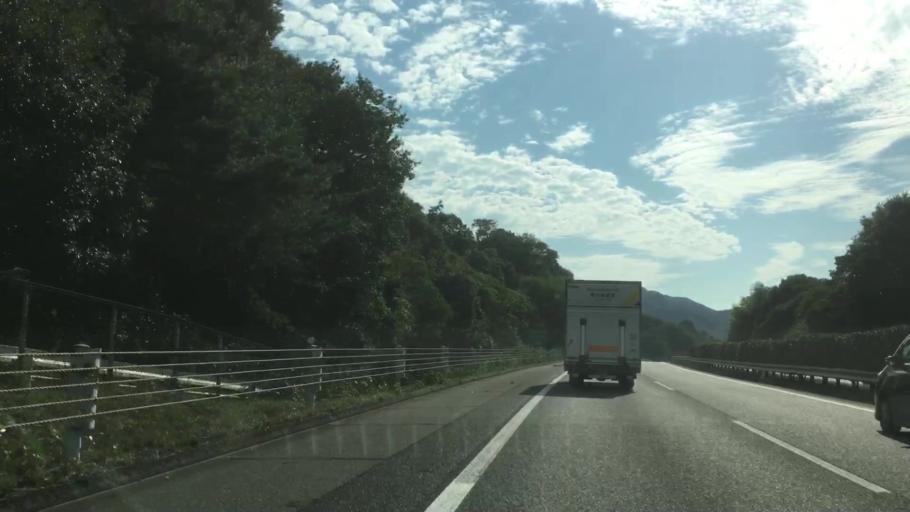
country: JP
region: Yamaguchi
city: Yanai
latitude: 34.0720
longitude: 132.0659
